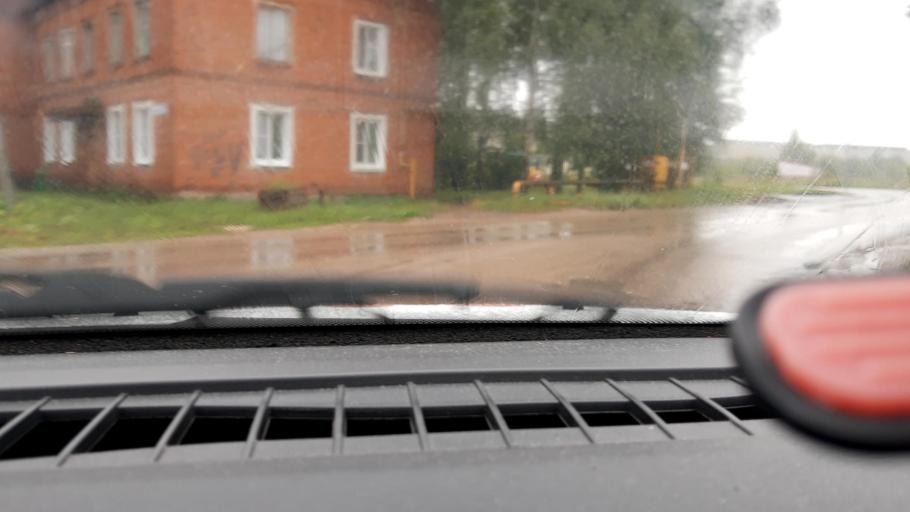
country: RU
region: Nizjnij Novgorod
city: Lyskovo
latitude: 56.0287
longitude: 45.0283
